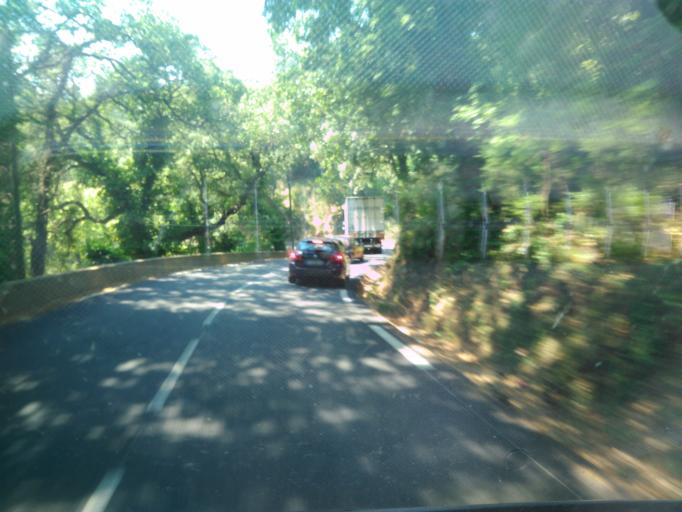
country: FR
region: Provence-Alpes-Cote d'Azur
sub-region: Departement du Var
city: La Garde-Freinet
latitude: 43.3286
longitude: 6.4716
